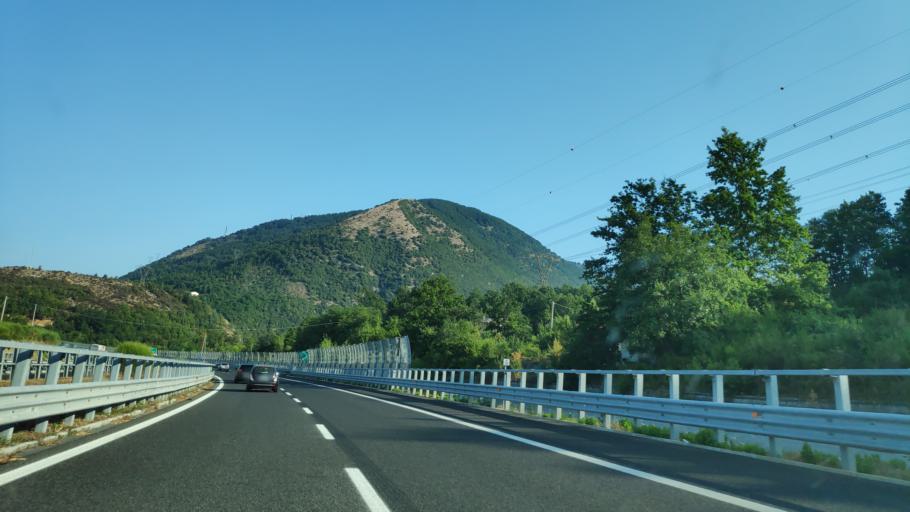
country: IT
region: Basilicate
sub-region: Provincia di Potenza
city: Lagonegro
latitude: 40.1213
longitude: 15.7839
